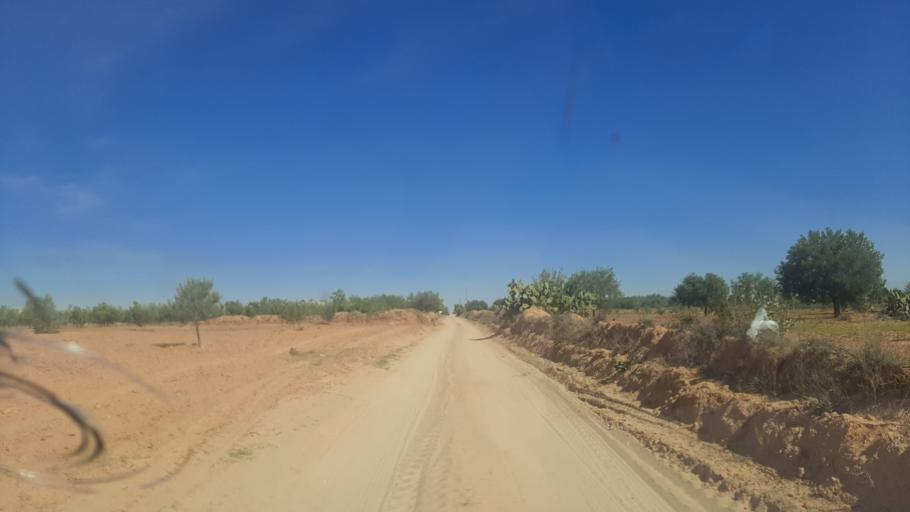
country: TN
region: Safaqis
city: Sfax
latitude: 34.8757
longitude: 10.5680
